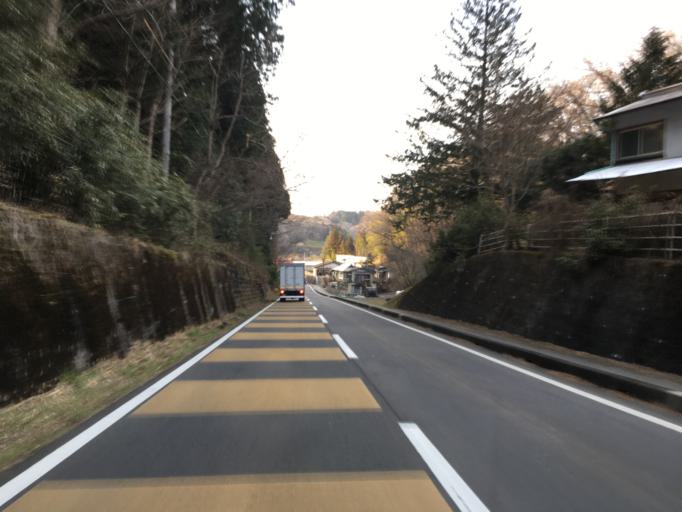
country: JP
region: Ibaraki
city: Daigo
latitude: 36.7851
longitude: 140.4233
